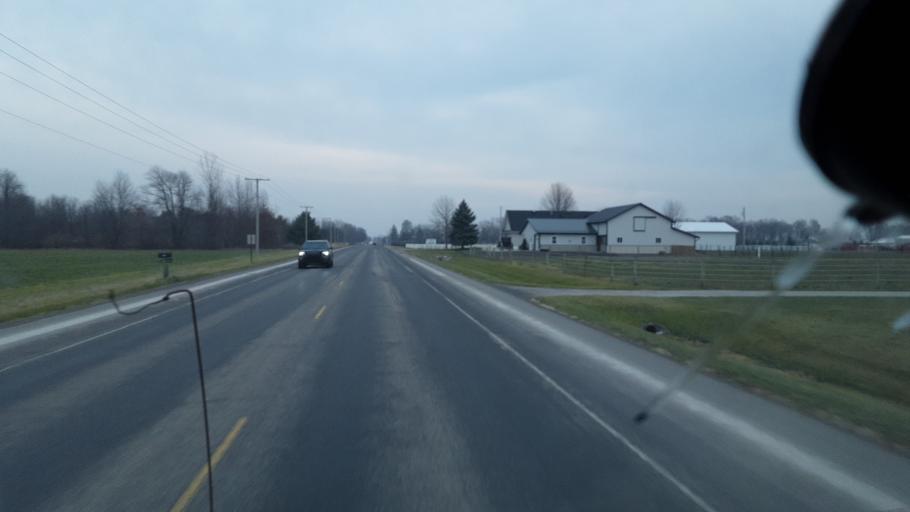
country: US
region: Indiana
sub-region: Elkhart County
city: Middlebury
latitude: 41.6761
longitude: -85.6071
